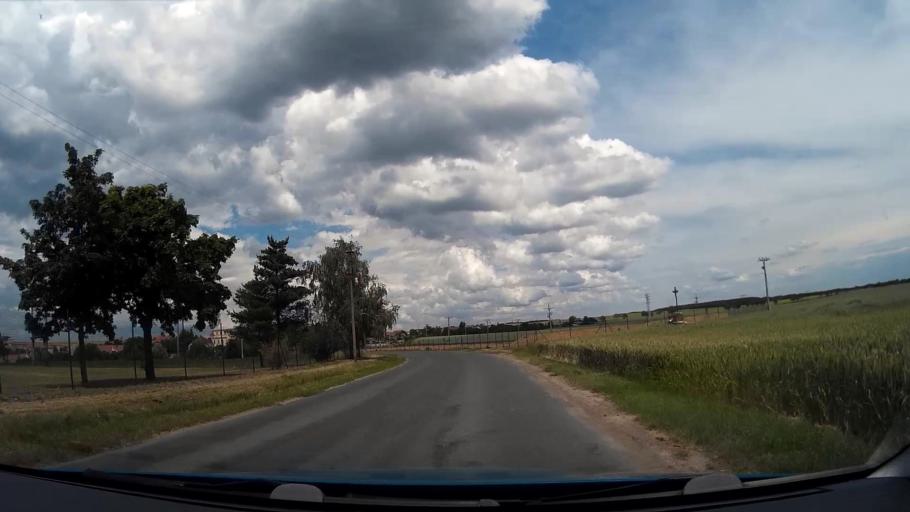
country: CZ
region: South Moravian
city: Orechov
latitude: 49.1067
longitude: 16.5263
